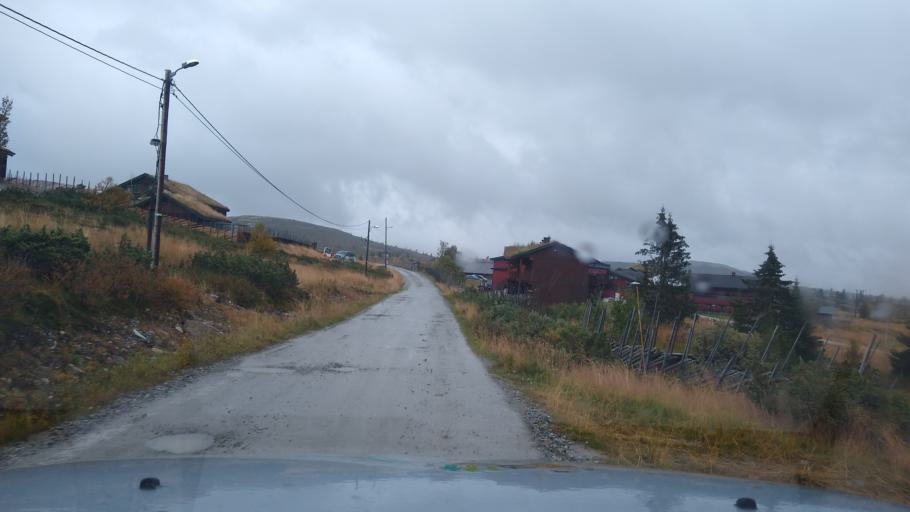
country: NO
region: Oppland
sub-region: Ringebu
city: Ringebu
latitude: 61.6722
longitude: 10.0989
